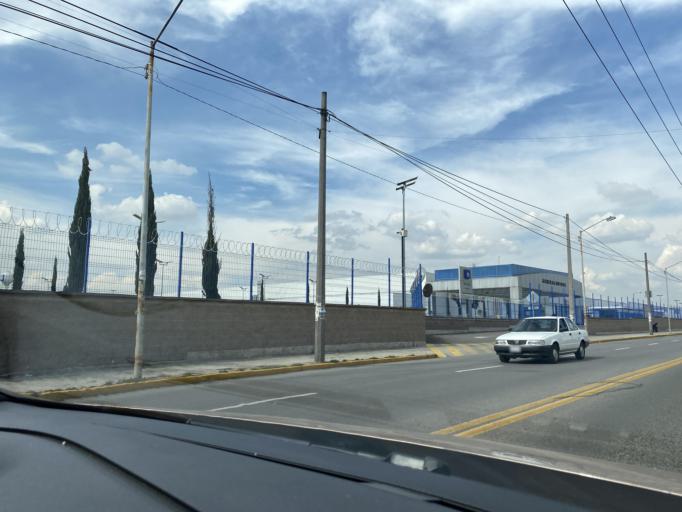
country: IN
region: Karnataka
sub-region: Dakshina Kannada
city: Puttur
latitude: 12.7370
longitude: 75.1858
